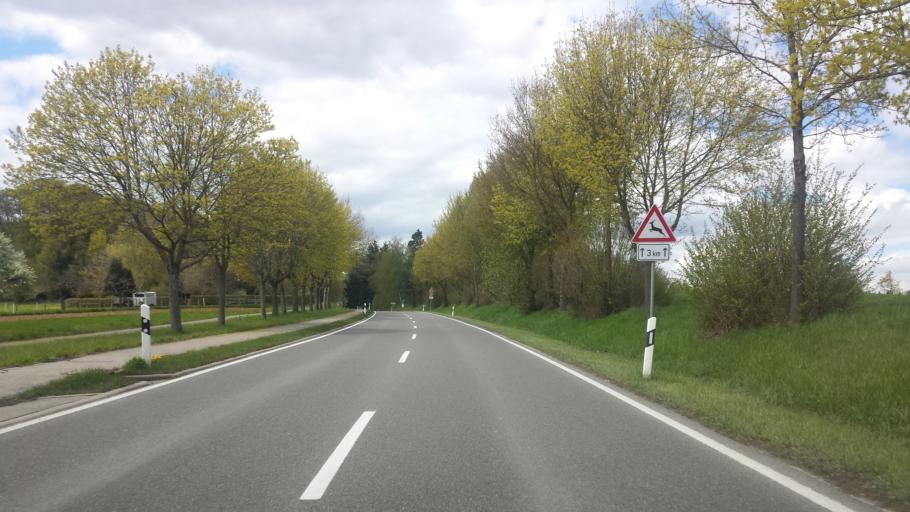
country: DE
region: Baden-Wuerttemberg
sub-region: Regierungsbezirk Stuttgart
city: Rutesheim
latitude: 48.8189
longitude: 8.9356
